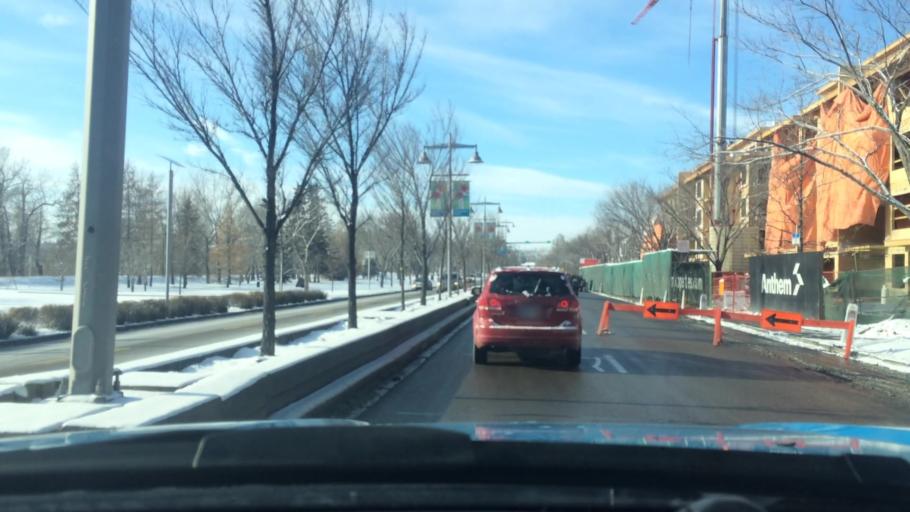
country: CA
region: Alberta
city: Calgary
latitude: 51.0517
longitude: -114.0873
